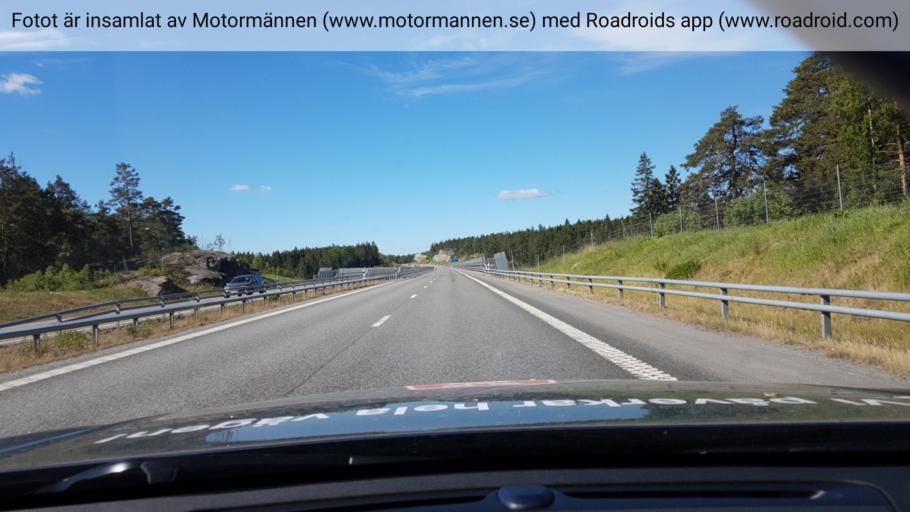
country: SE
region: Stockholm
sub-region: Nynashamns Kommun
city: Osmo
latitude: 59.0411
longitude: 17.9714
